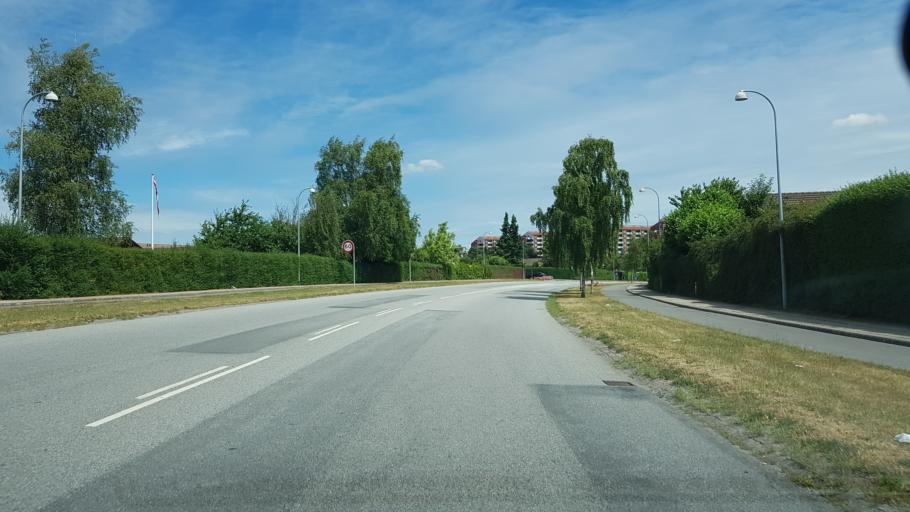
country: DK
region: Capital Region
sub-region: Brondby Kommune
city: Brondbyvester
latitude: 55.6605
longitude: 12.4331
